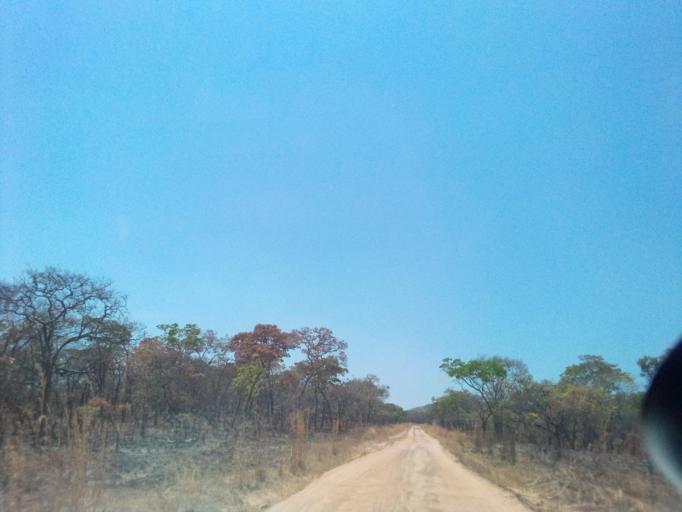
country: ZM
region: Northern
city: Mpika
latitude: -12.2539
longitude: 30.6914
